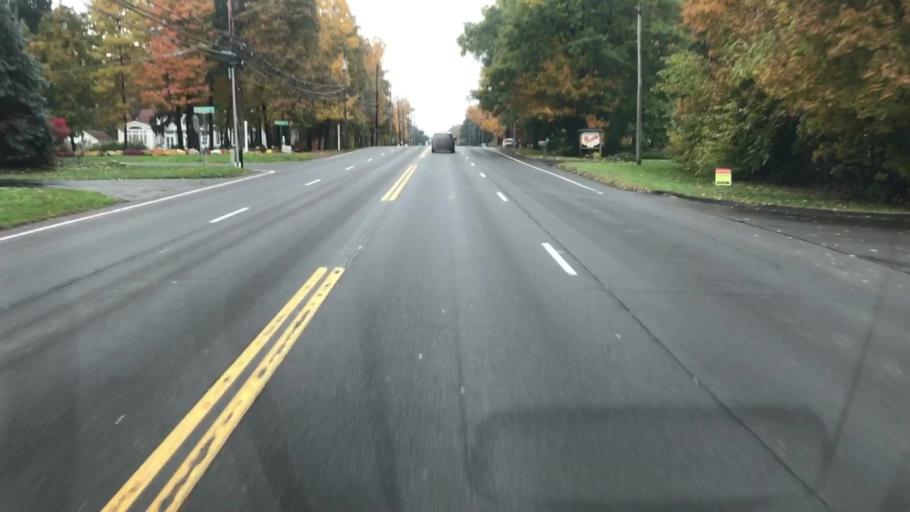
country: US
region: New York
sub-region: Onondaga County
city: Fayetteville
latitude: 43.0287
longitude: -76.0309
